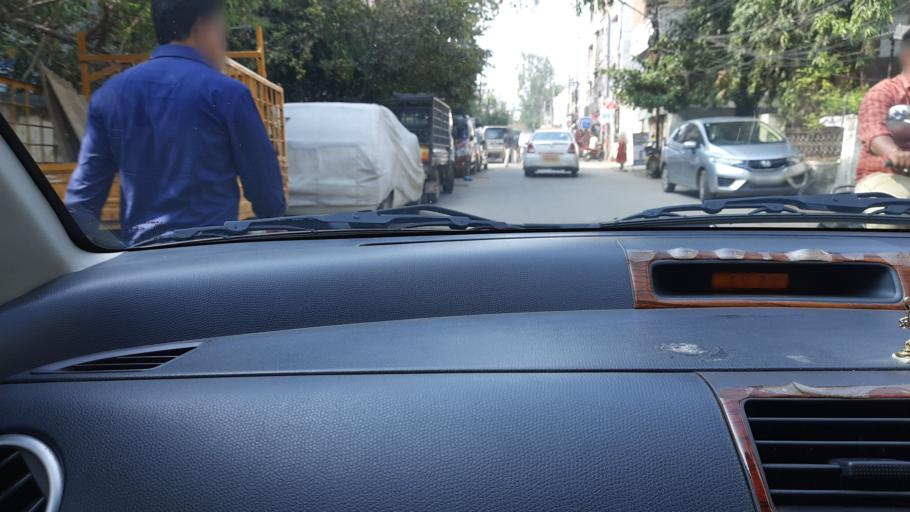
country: IN
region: Telangana
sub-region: Rangareddi
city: Quthbullapur
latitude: 17.4459
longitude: 78.4610
